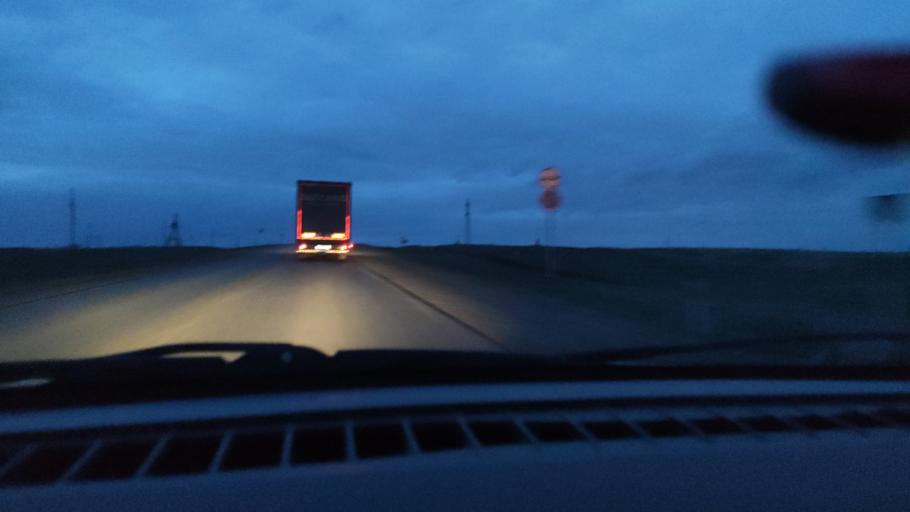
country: RU
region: Orenburg
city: Tatarskaya Kargala
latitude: 51.9547
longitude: 55.1832
